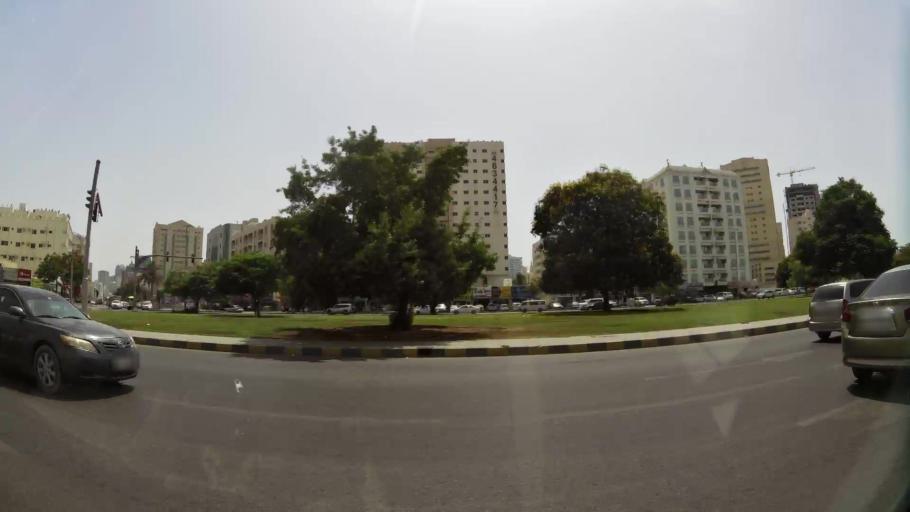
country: AE
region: Ash Shariqah
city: Sharjah
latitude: 25.3475
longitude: 55.3989
